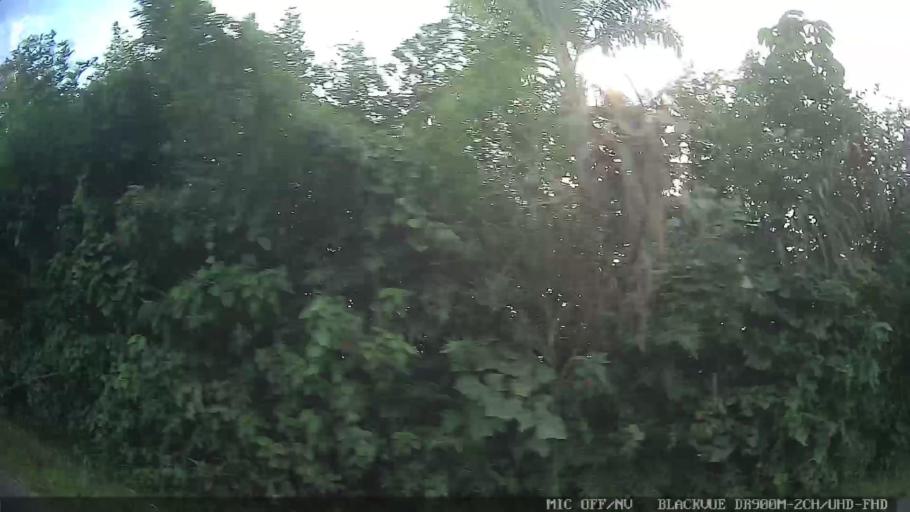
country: BR
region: Sao Paulo
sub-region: Mogi das Cruzes
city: Mogi das Cruzes
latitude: -23.5548
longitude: -46.1487
